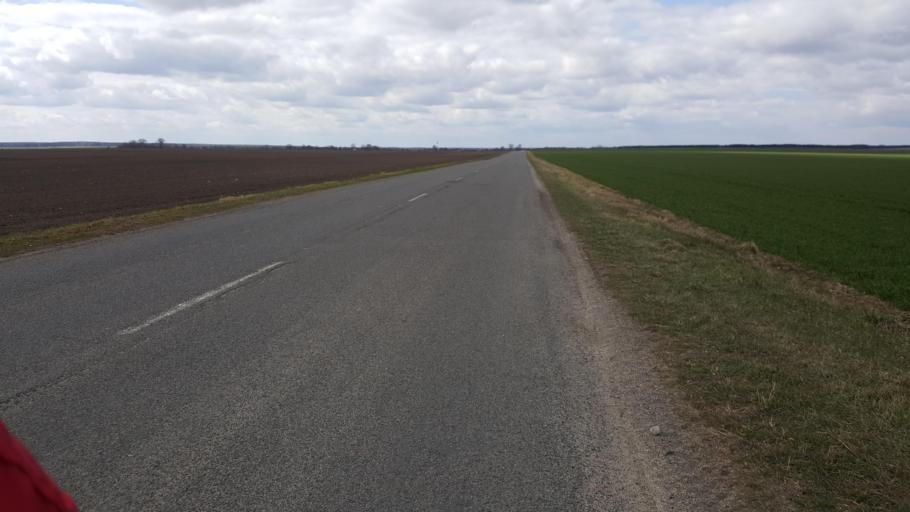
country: BY
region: Brest
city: Vysokaye
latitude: 52.3699
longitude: 23.5573
